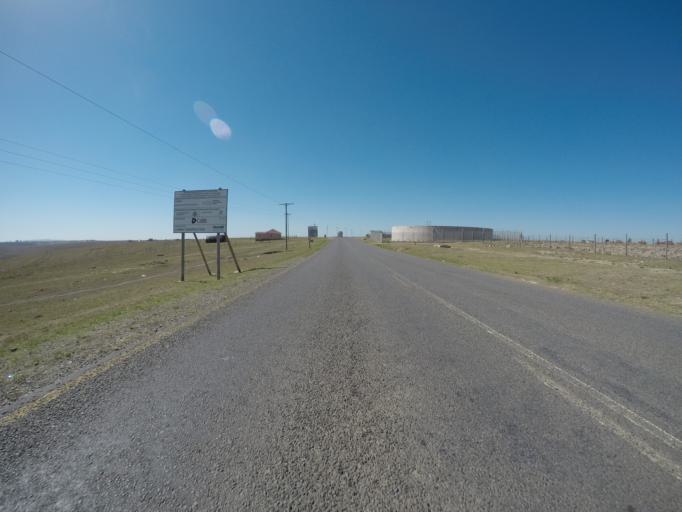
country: ZA
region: Eastern Cape
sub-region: OR Tambo District Municipality
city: Mthatha
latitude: -31.8862
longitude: 28.7609
